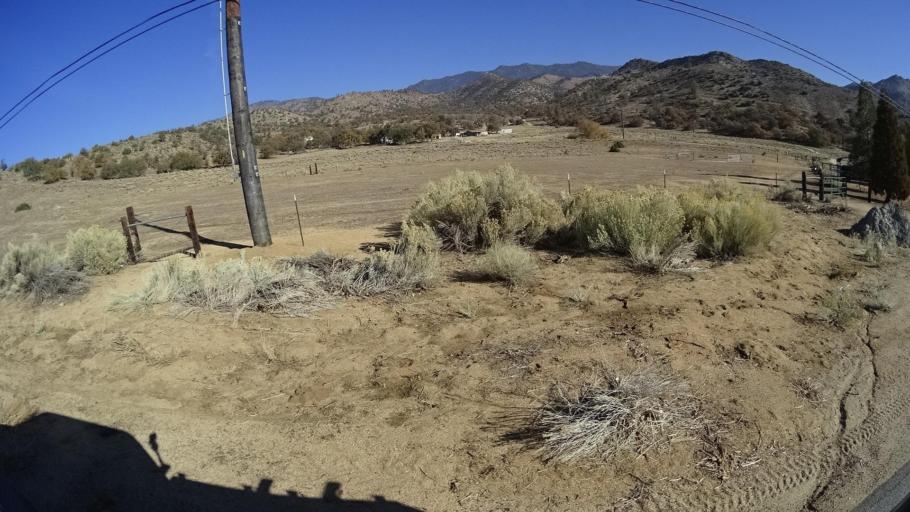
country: US
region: California
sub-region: Kern County
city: Tehachapi
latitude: 35.3670
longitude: -118.3882
